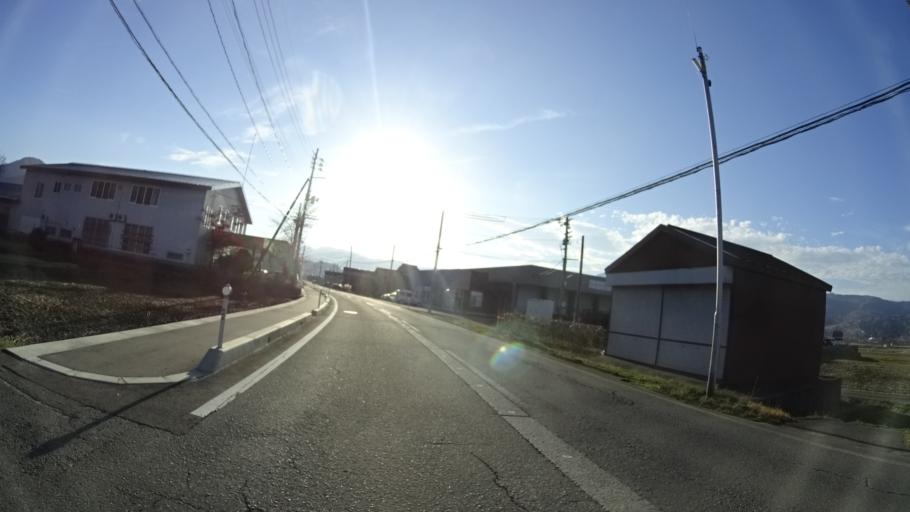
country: JP
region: Niigata
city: Shiozawa
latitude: 37.0213
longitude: 138.8636
